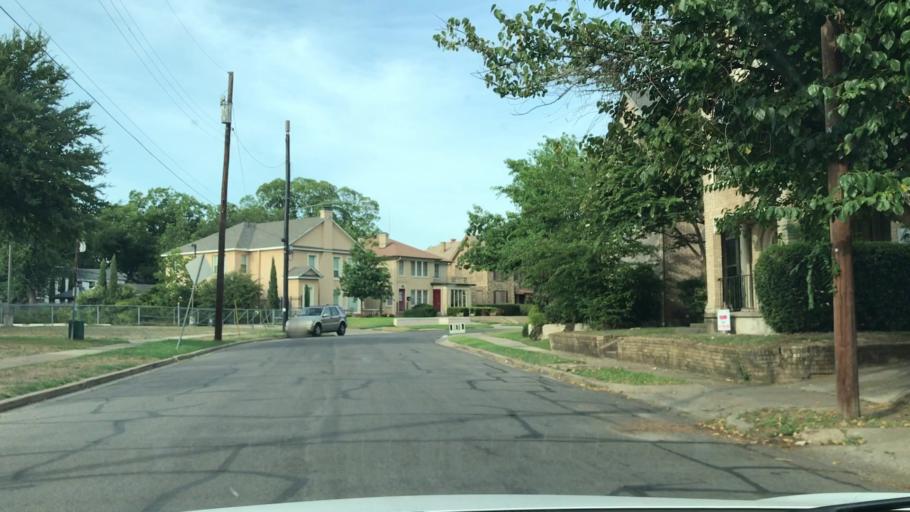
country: US
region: Texas
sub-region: Dallas County
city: Highland Park
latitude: 32.8203
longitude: -96.8096
